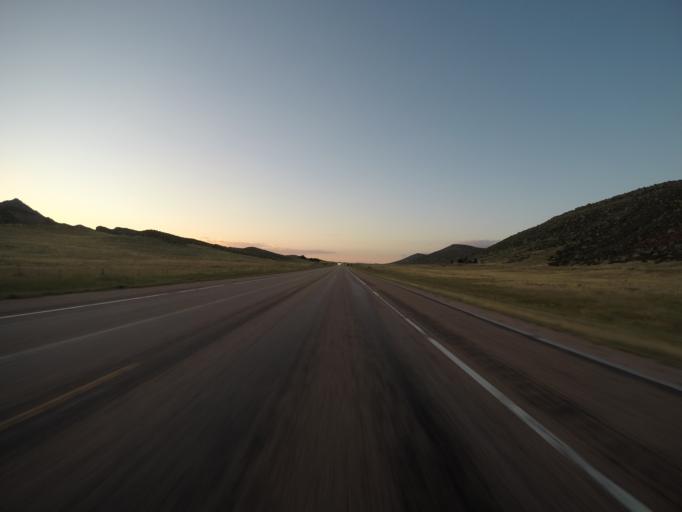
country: US
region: Colorado
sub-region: Larimer County
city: Laporte
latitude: 40.7232
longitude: -105.1717
